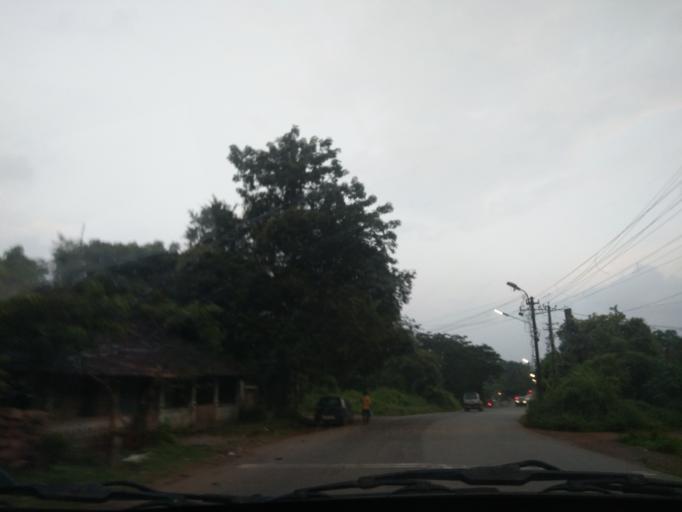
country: IN
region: Goa
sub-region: South Goa
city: Davorlim
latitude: 15.2412
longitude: 74.0201
